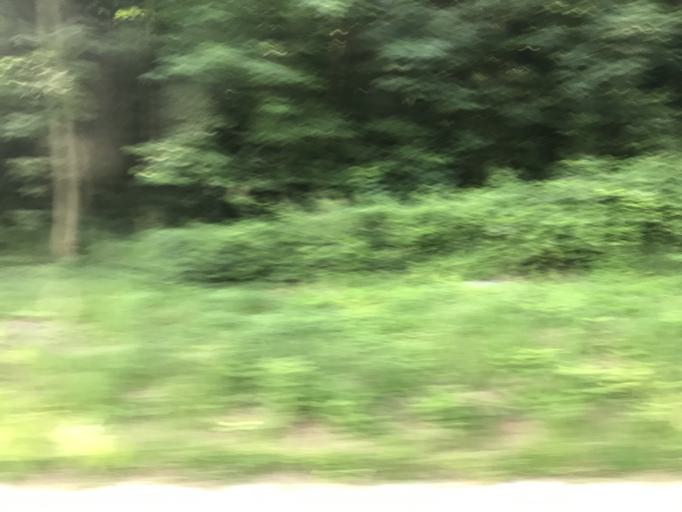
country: ES
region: Basque Country
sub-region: Provincia de Guipuzcoa
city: Arama
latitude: 43.0638
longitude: -2.1678
